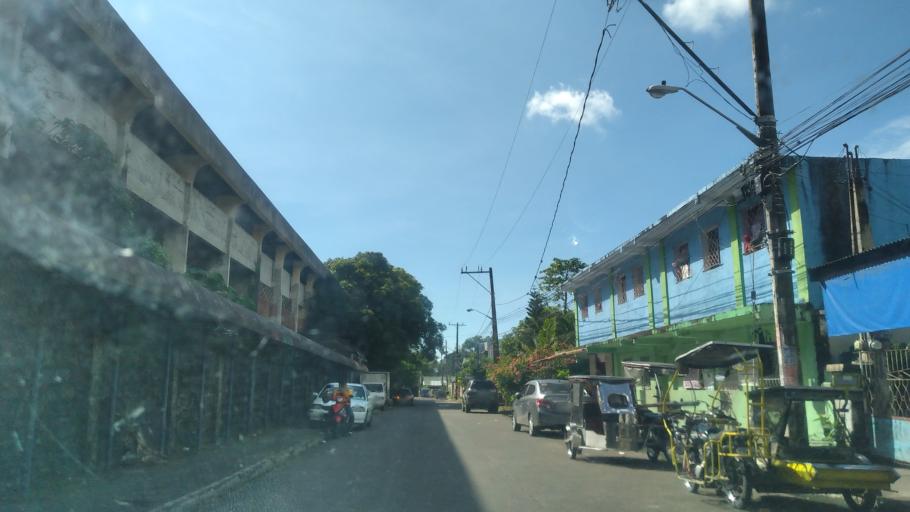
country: PH
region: Calabarzon
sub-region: Province of Quezon
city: Lucena
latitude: 13.9328
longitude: 121.6045
